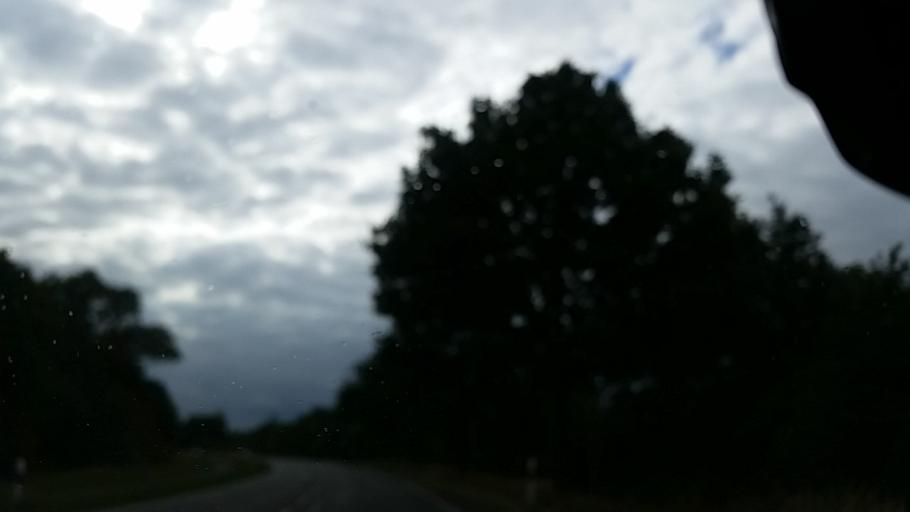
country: DE
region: Lower Saxony
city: Wolfsburg
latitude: 52.4268
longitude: 10.8409
